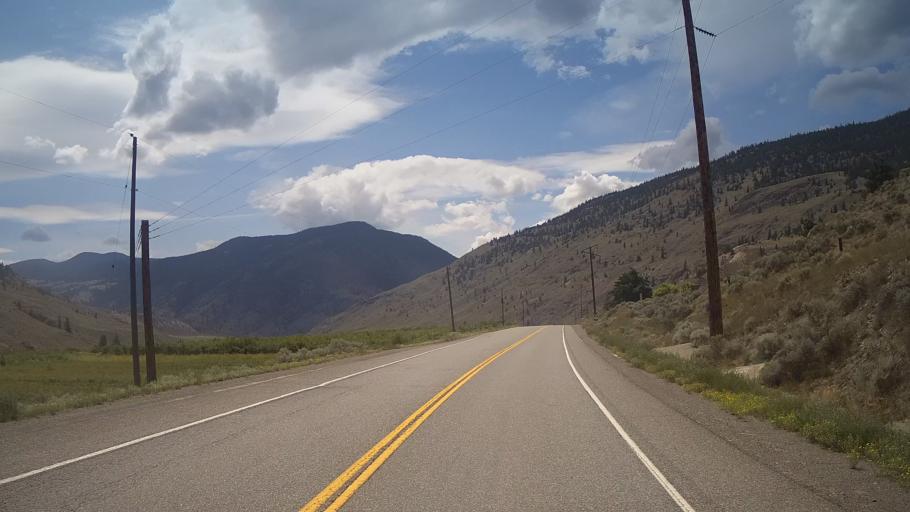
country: CA
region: British Columbia
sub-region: Thompson-Nicola Regional District
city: Ashcroft
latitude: 50.4591
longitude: -121.3030
